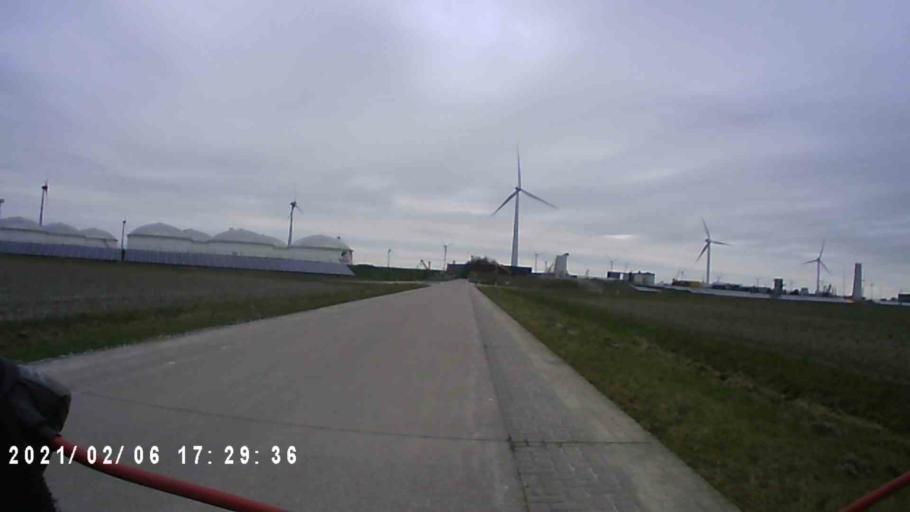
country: NL
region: Groningen
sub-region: Gemeente Appingedam
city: Appingedam
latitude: 53.4430
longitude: 6.8030
